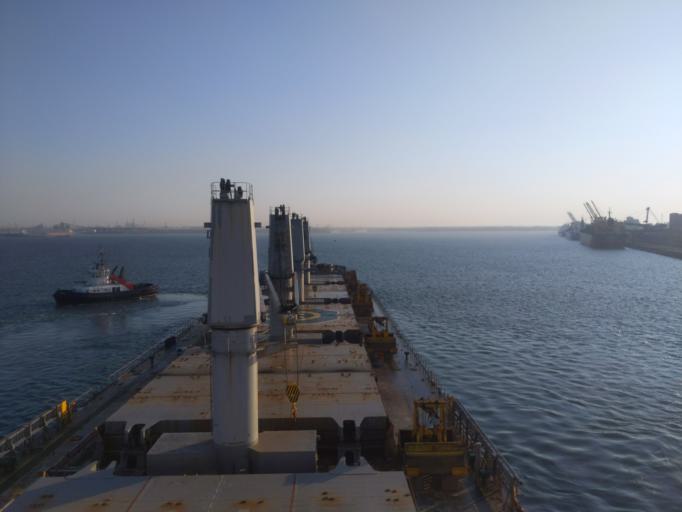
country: ZA
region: KwaZulu-Natal
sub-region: uThungulu District Municipality
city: Richards Bay
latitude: -28.8206
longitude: 32.0459
